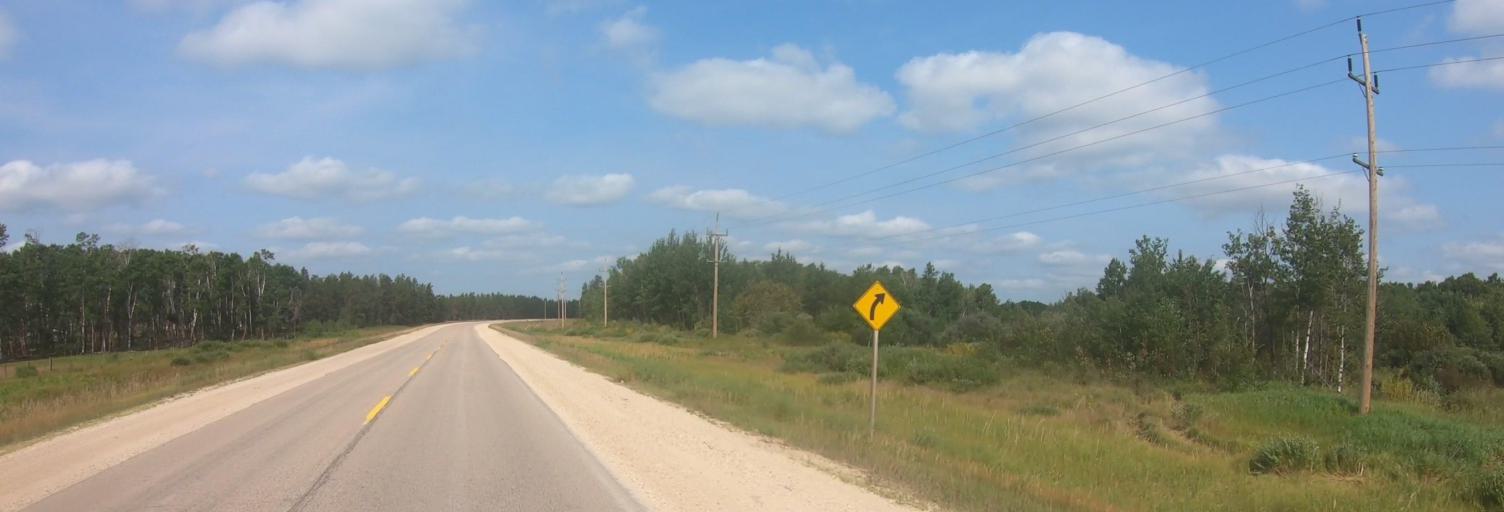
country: CA
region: Manitoba
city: La Broquerie
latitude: 49.2357
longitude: -96.3414
